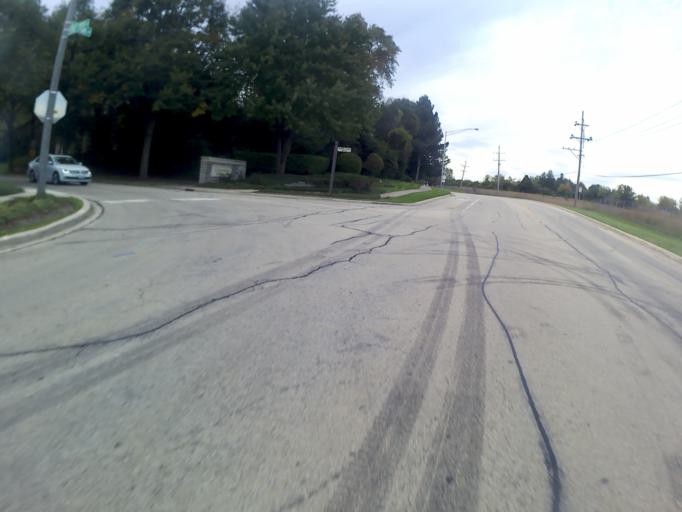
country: US
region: Illinois
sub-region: DuPage County
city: Lisle
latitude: 41.8143
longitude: -88.0940
